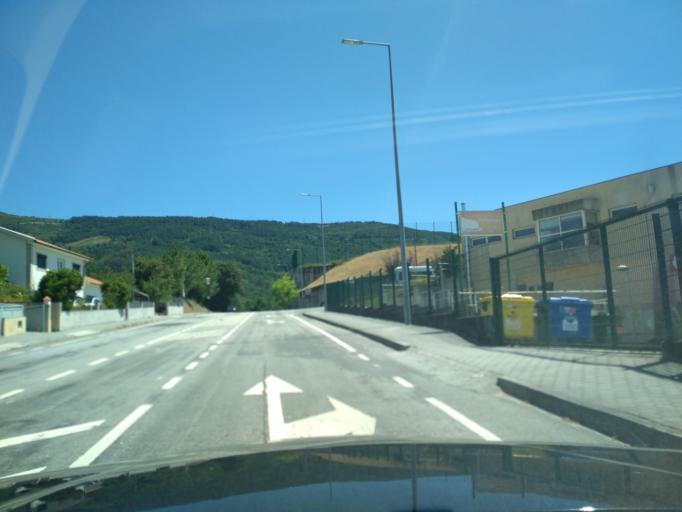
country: PT
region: Vila Real
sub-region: Ribeira de Pena
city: Sobreira
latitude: 41.5261
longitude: -7.7925
